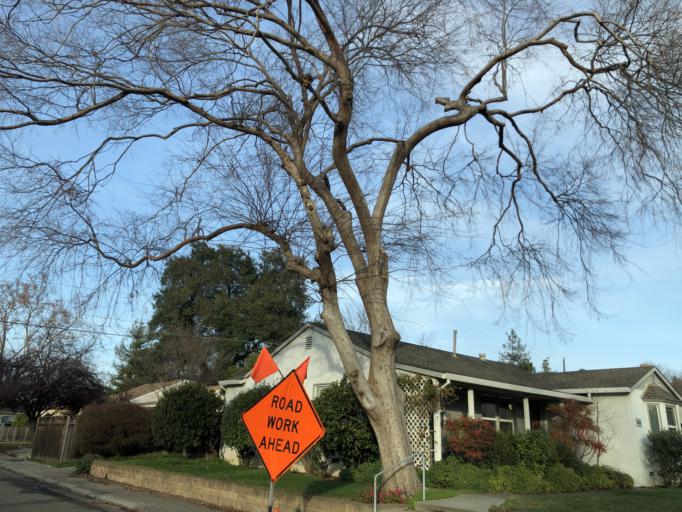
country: US
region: California
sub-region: Sacramento County
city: Parkway
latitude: 38.5489
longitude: -121.4342
